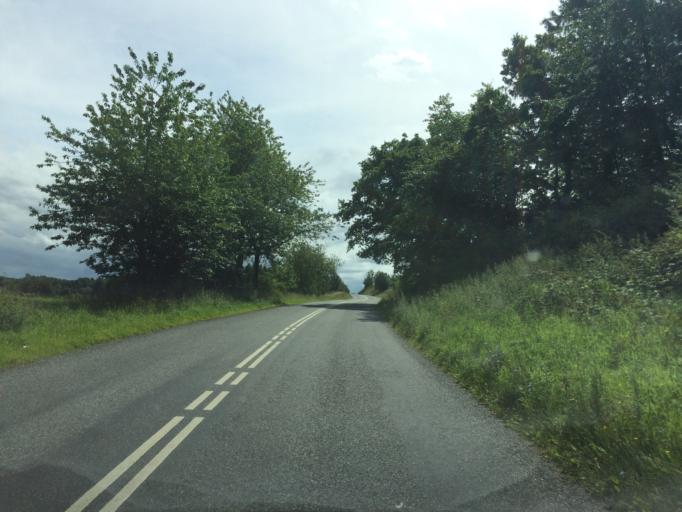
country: DK
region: South Denmark
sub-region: Faaborg-Midtfyn Kommune
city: Faaborg
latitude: 55.1821
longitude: 10.2495
